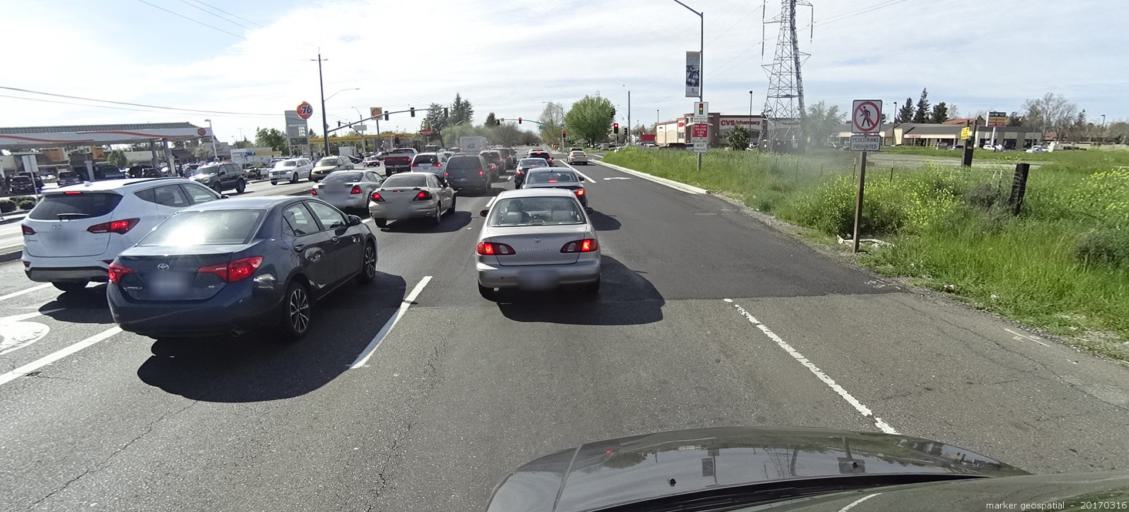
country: US
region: California
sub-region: Sacramento County
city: Florin
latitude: 38.4743
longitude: -121.4261
